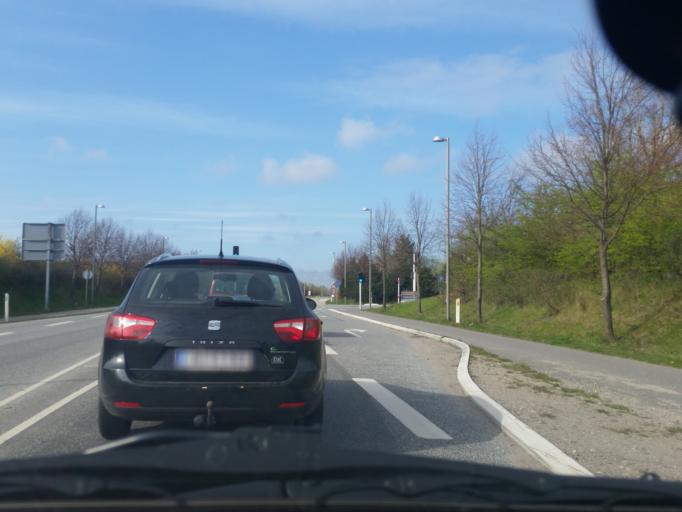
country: DK
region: Zealand
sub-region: Soro Kommune
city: Soro
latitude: 55.4568
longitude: 11.5618
